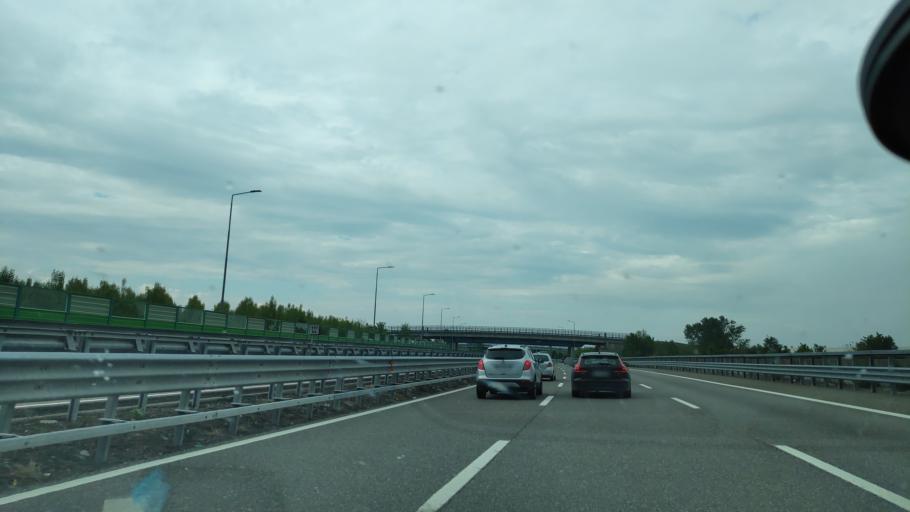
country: IT
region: Piedmont
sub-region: Provincia di Alessandria
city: Castelnuovo Scrivia
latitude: 44.9757
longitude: 8.8962
